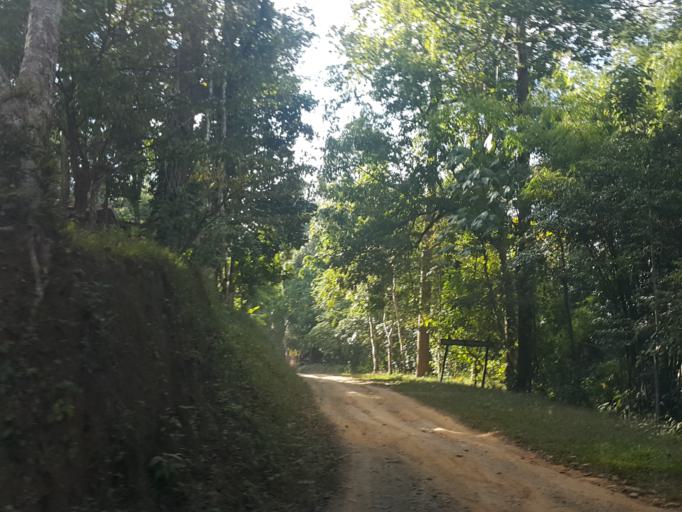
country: TH
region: Chiang Mai
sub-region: Amphoe Chiang Dao
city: Chiang Dao
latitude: 19.4036
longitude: 98.9233
